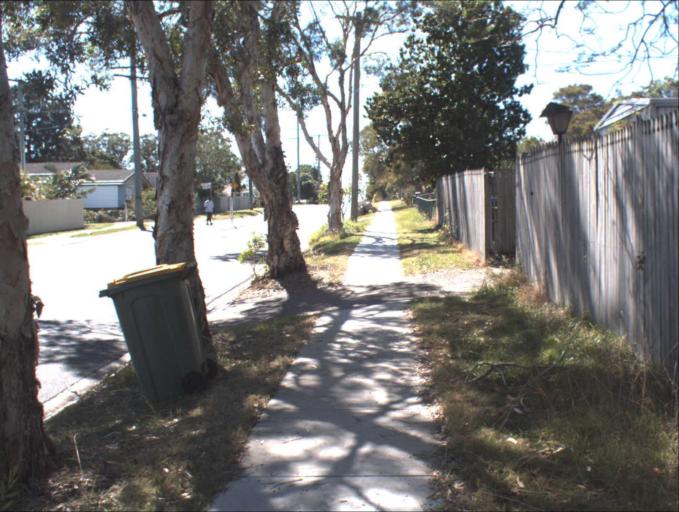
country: AU
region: Queensland
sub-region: Logan
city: Logan City
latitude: -27.6320
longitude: 153.1194
